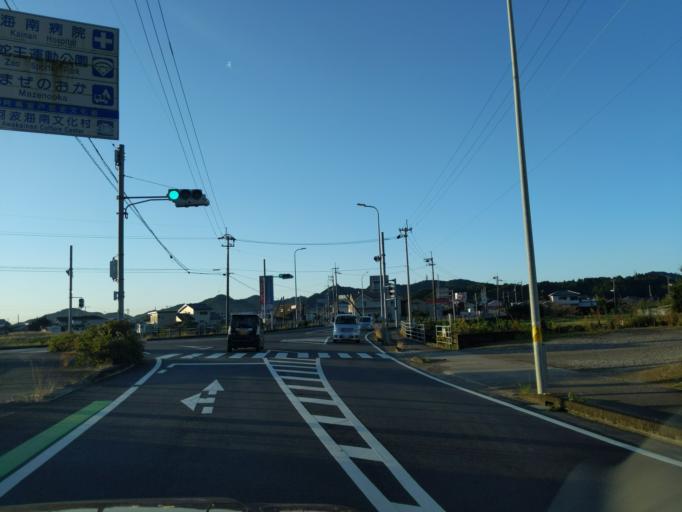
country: JP
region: Kochi
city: Muroto-misakicho
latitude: 33.6128
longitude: 134.3534
